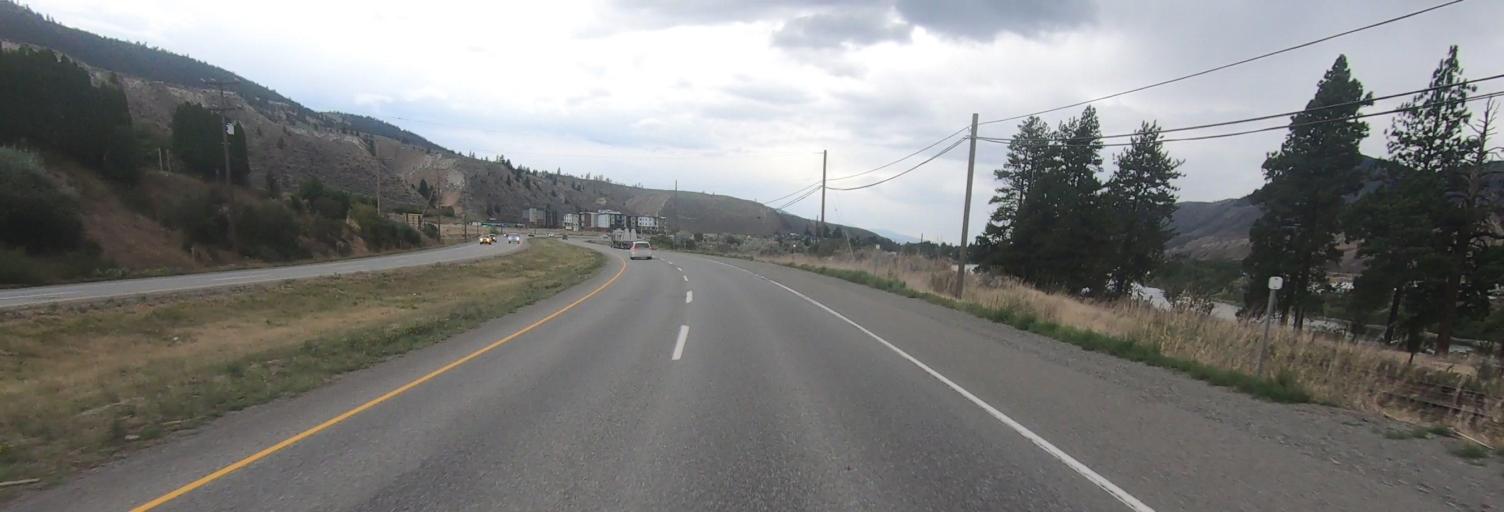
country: CA
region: British Columbia
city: Kamloops
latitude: 50.6718
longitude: -120.2144
